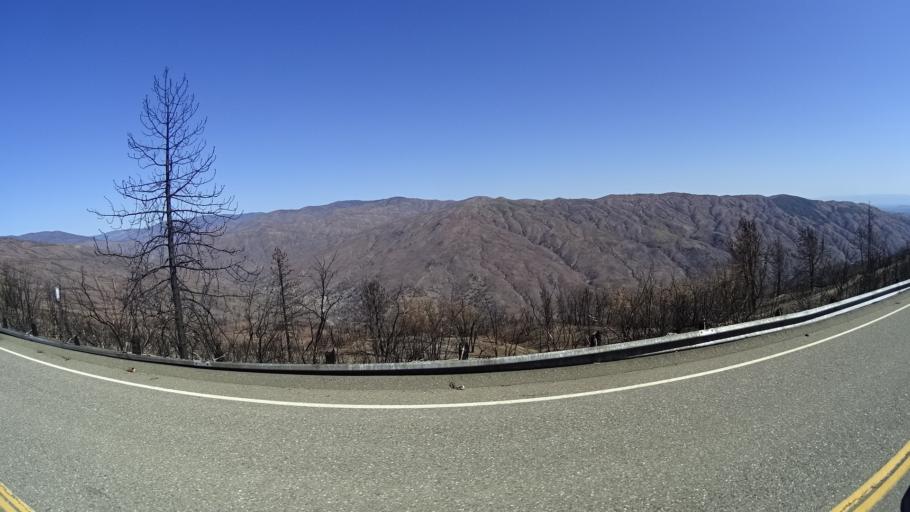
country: US
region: California
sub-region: Tehama County
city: Rancho Tehama Reserve
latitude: 39.6676
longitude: -122.6734
